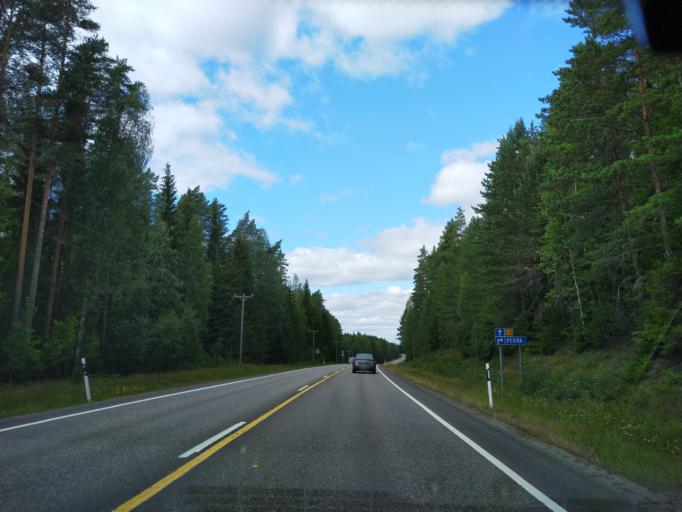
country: FI
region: Haeme
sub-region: Haemeenlinna
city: Renko
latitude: 60.7522
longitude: 24.3087
